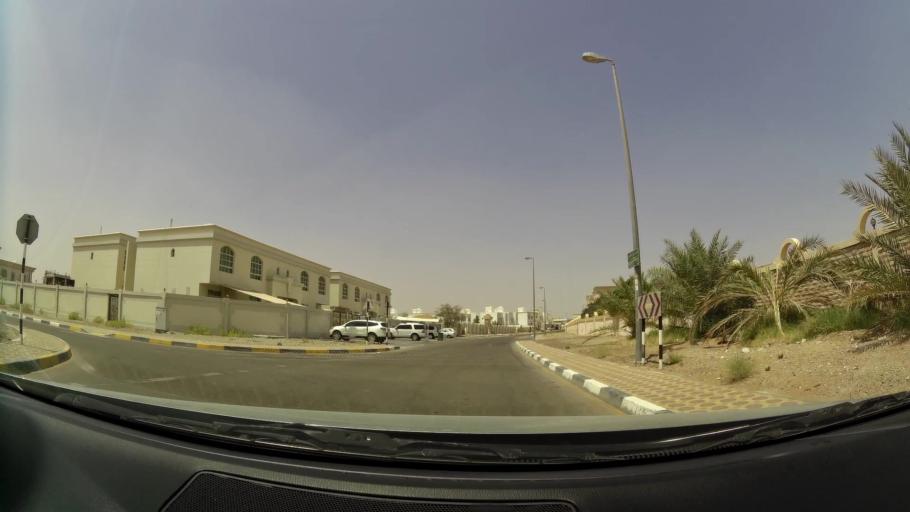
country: AE
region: Abu Dhabi
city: Al Ain
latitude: 24.2616
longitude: 55.7012
